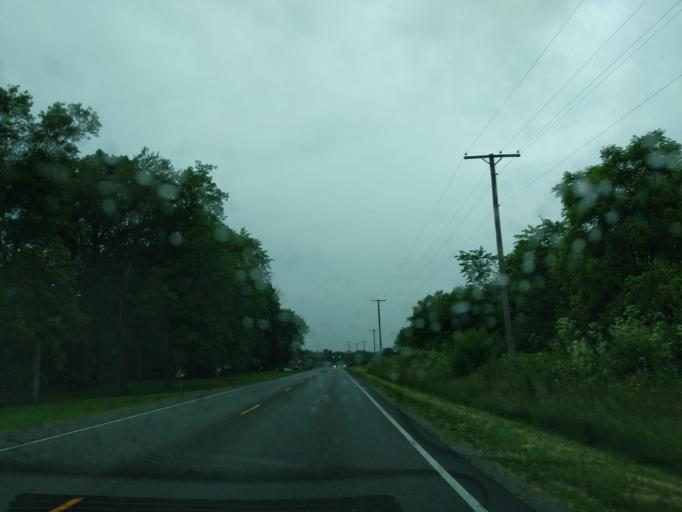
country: US
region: Indiana
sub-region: Madison County
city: Chesterfield
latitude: 40.0933
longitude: -85.6173
